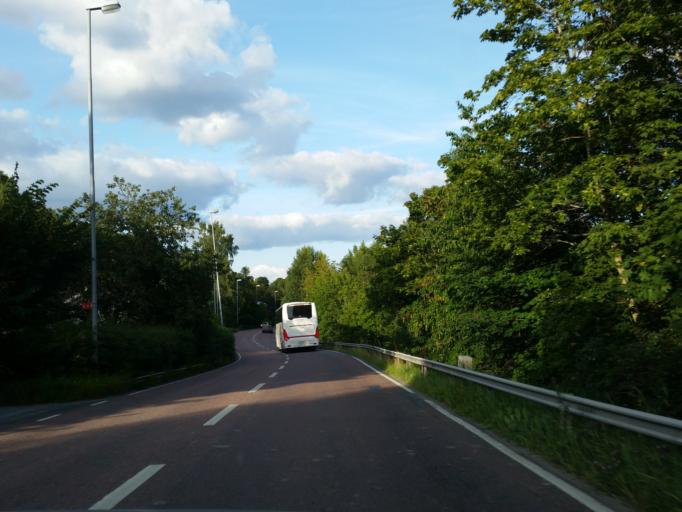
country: SE
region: Stockholm
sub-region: Sodertalje Kommun
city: Pershagen
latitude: 59.0876
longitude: 17.5687
